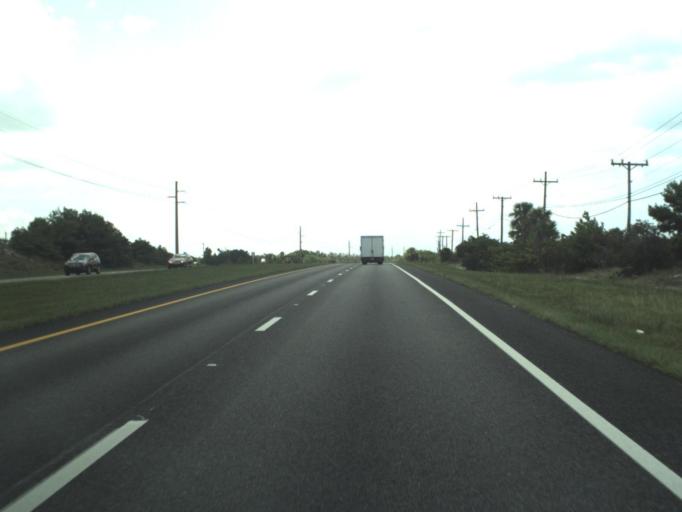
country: US
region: Florida
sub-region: Martin County
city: Hobe Sound
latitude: 27.0207
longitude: -80.1072
